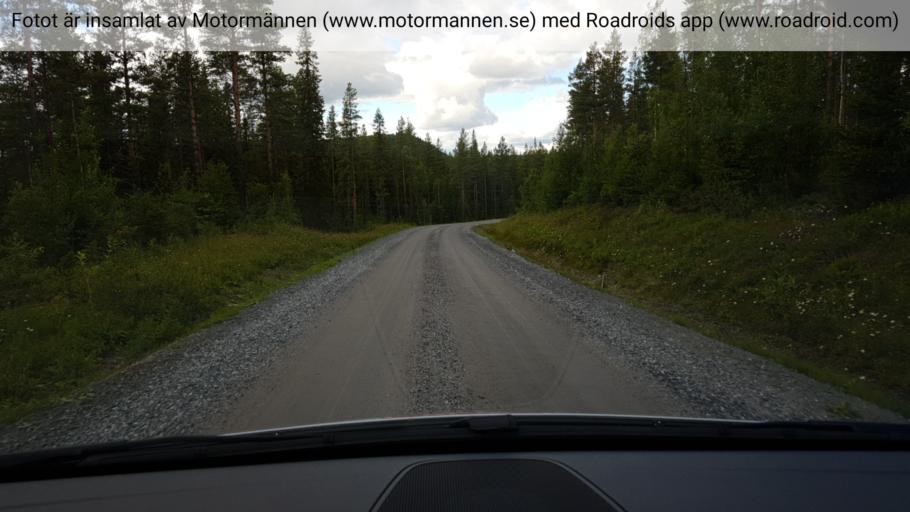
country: SE
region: Jaemtland
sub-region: Braecke Kommun
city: Braecke
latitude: 62.9621
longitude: 15.7351
